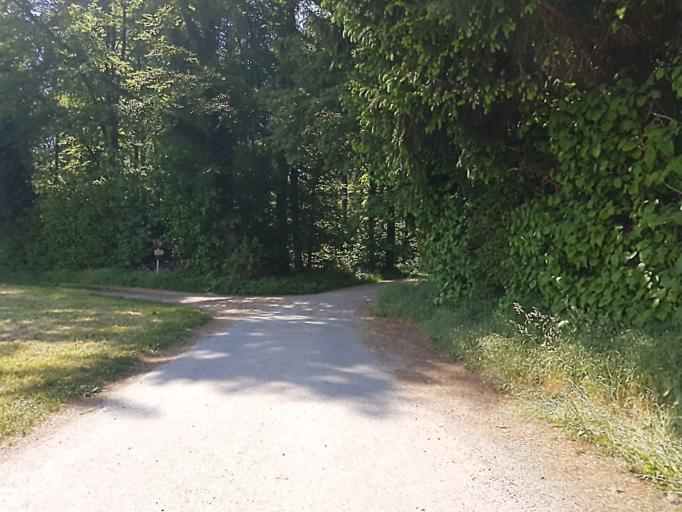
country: CH
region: Thurgau
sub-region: Arbon District
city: Uttwil
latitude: 47.5740
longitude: 9.3131
